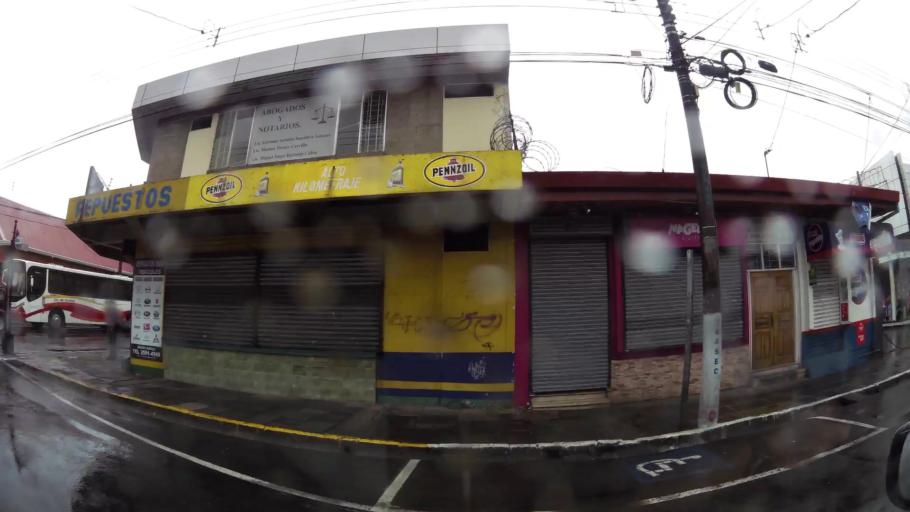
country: CR
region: Cartago
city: Cartago
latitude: 9.8644
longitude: -83.9183
